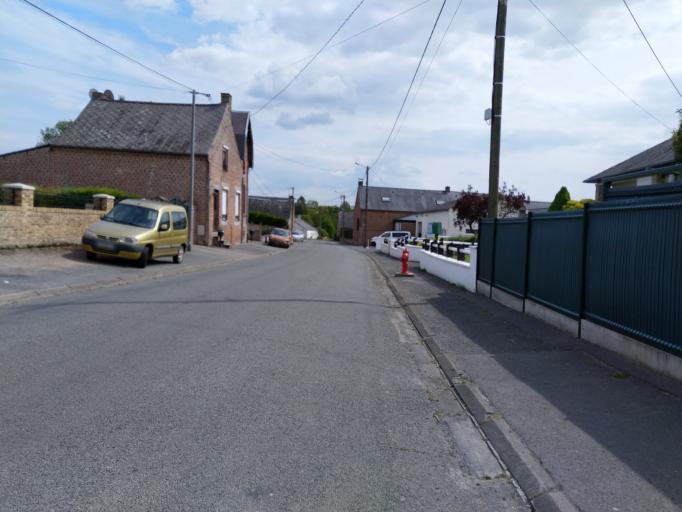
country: FR
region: Picardie
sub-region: Departement de l'Aisne
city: Boue
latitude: 50.0140
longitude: 3.6936
